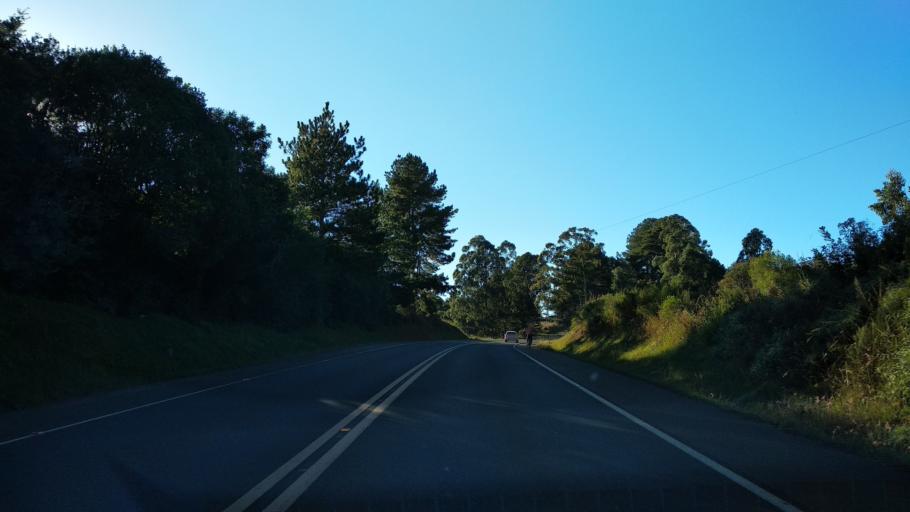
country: BR
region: Santa Catarina
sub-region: Lages
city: Lages
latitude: -27.7855
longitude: -50.4429
